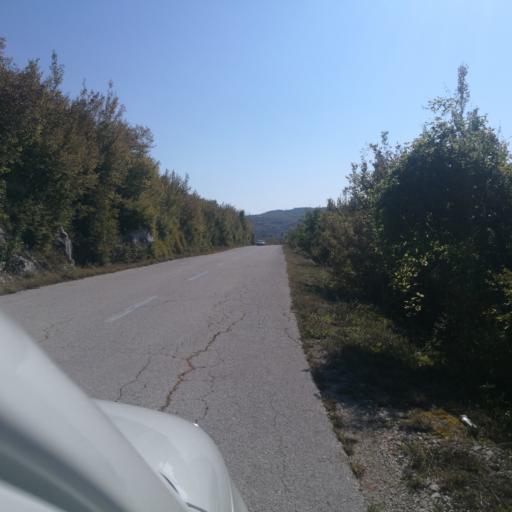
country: HR
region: Splitsko-Dalmatinska
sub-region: Grad Omis
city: Omis
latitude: 43.5205
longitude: 16.7536
